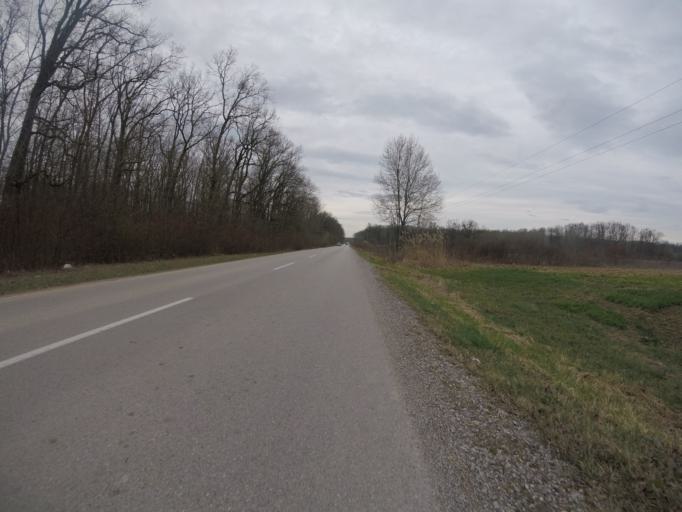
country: HR
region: Zagrebacka
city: Lukavec
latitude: 45.6944
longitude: 15.9834
